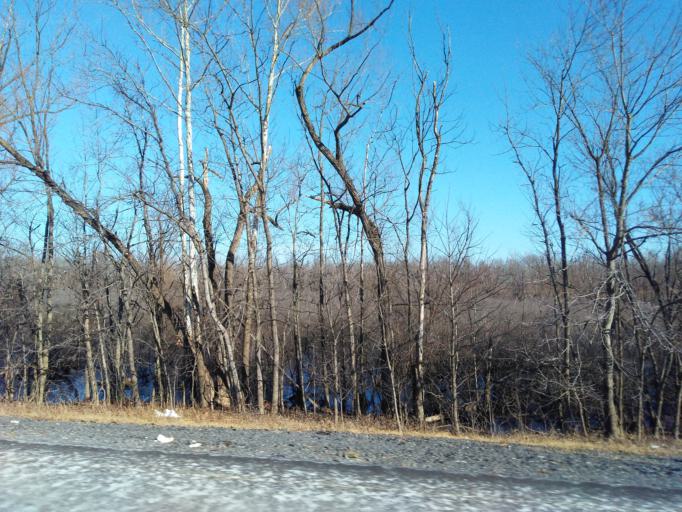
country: US
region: Illinois
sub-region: Williamson County
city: Marion
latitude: 37.6982
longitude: -88.9654
